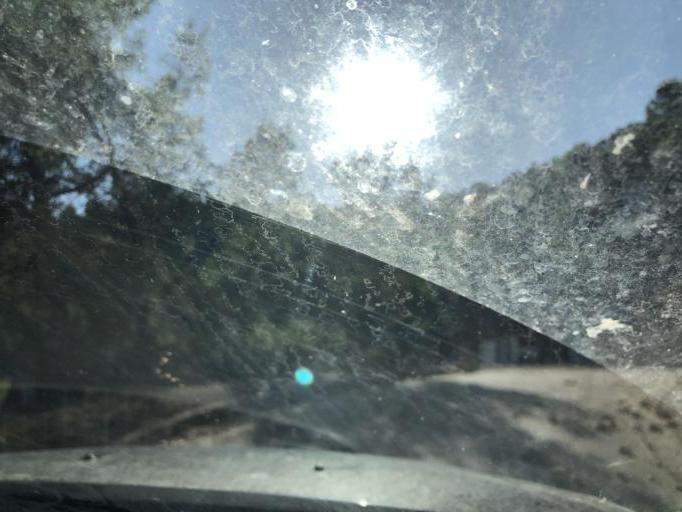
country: ES
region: Balearic Islands
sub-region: Illes Balears
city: Camp de Mar
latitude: 39.5379
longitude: 2.4041
